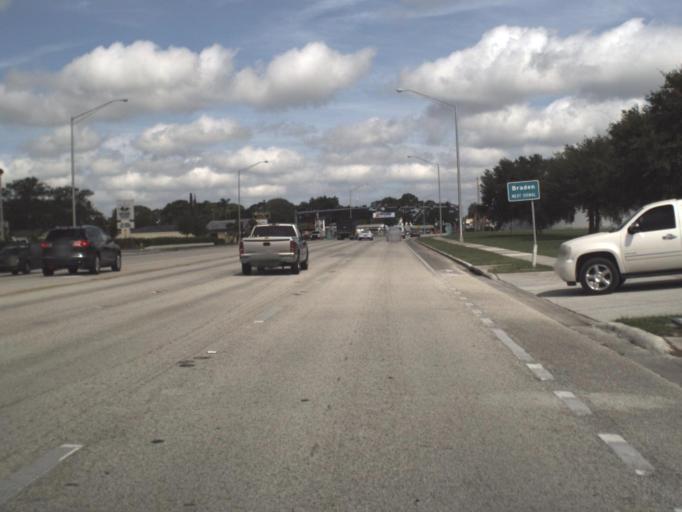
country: US
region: Florida
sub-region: Manatee County
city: Whitfield
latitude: 27.3947
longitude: -82.5622
